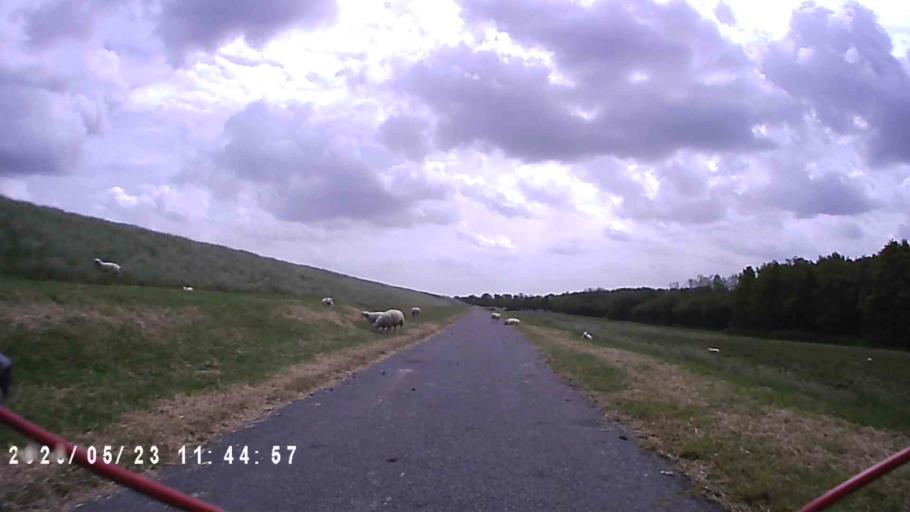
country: NL
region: Groningen
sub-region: Gemeente Delfzijl
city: Delfzijl
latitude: 53.3033
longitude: 7.0198
